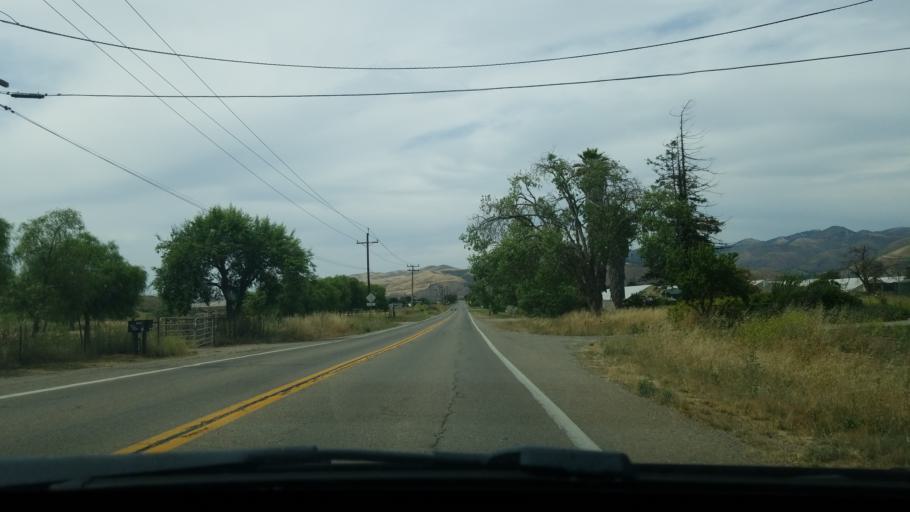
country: US
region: California
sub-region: Santa Barbara County
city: Orcutt
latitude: 34.8838
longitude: -120.3150
